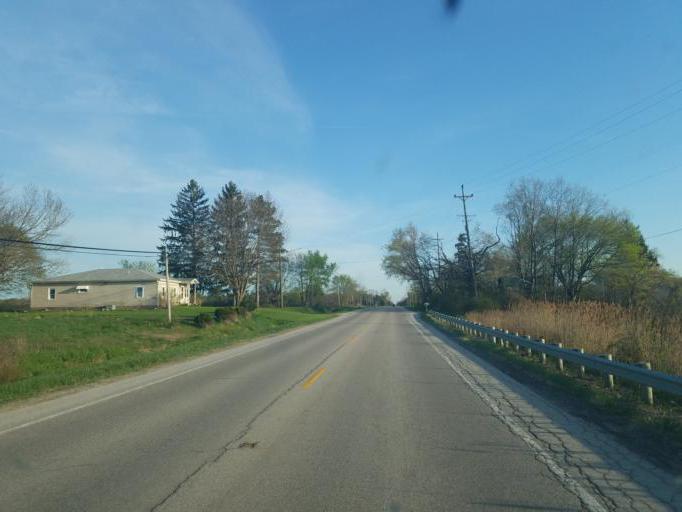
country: US
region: Ohio
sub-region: Ashtabula County
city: Conneaut
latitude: 41.8280
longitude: -80.5723
